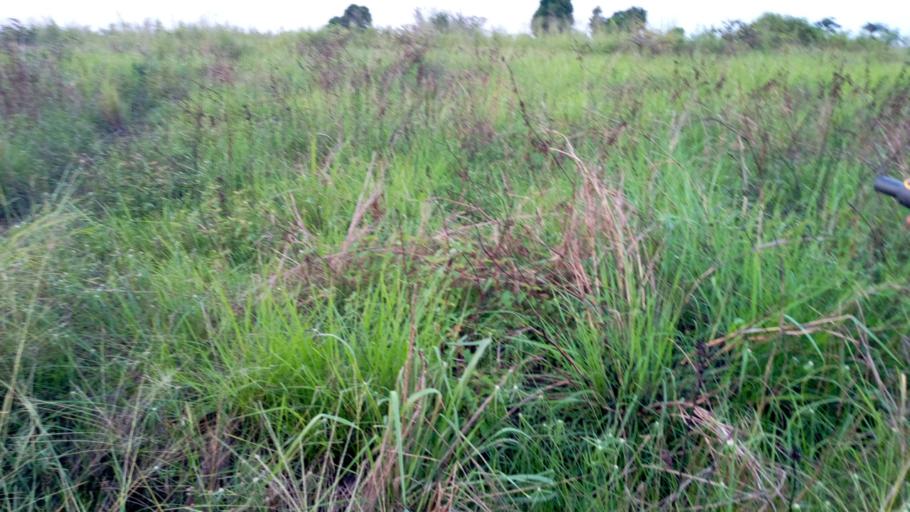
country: CD
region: Bandundu
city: Bandundu
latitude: -3.2725
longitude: 17.3849
